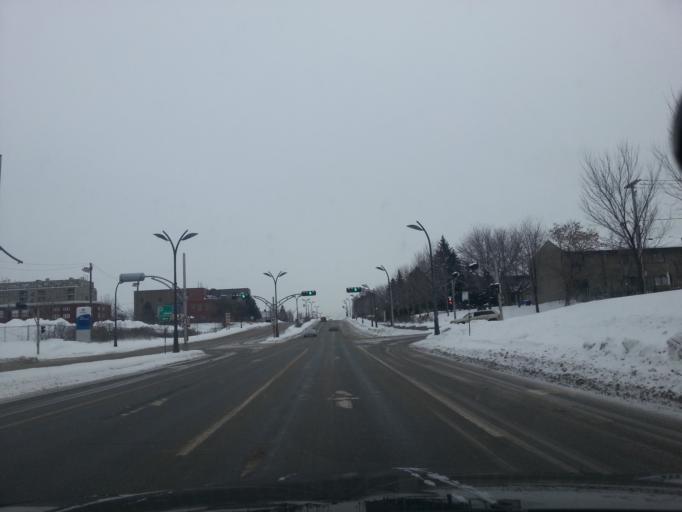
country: CA
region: Ontario
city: Ottawa
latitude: 45.4322
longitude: -75.7267
